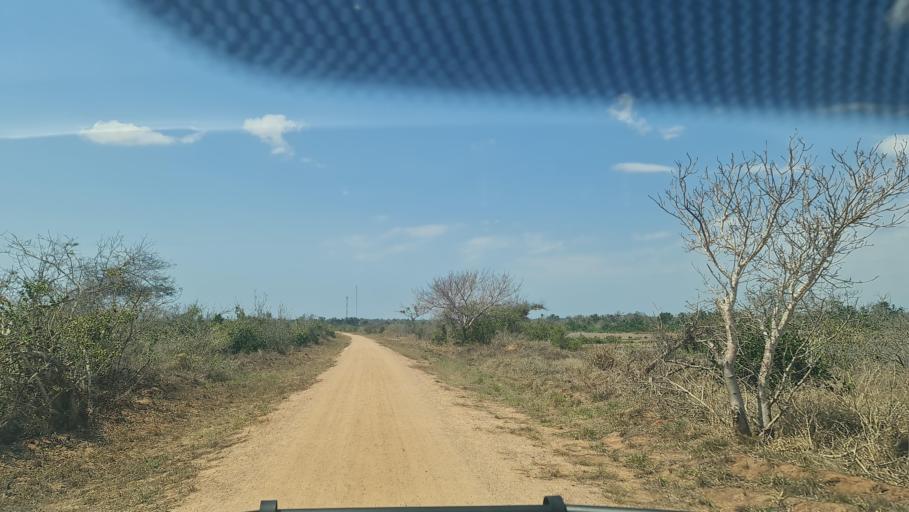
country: MZ
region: Nampula
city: Ilha de Mocambique
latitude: -15.1872
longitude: 40.5189
